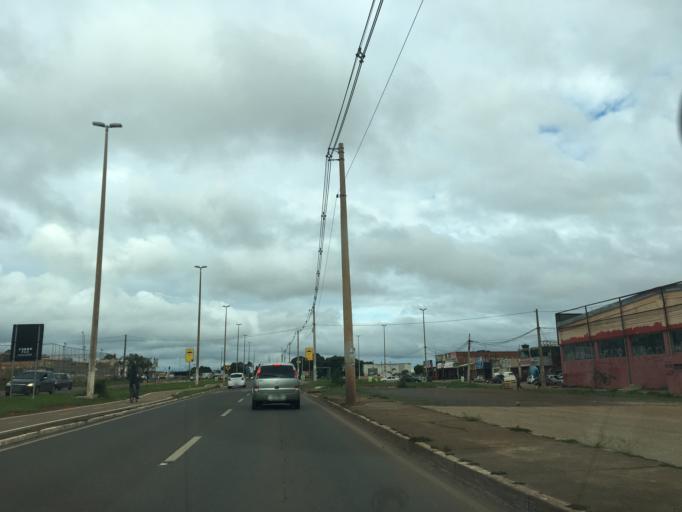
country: BR
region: Goias
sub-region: Luziania
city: Luziania
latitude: -16.0474
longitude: -48.0332
